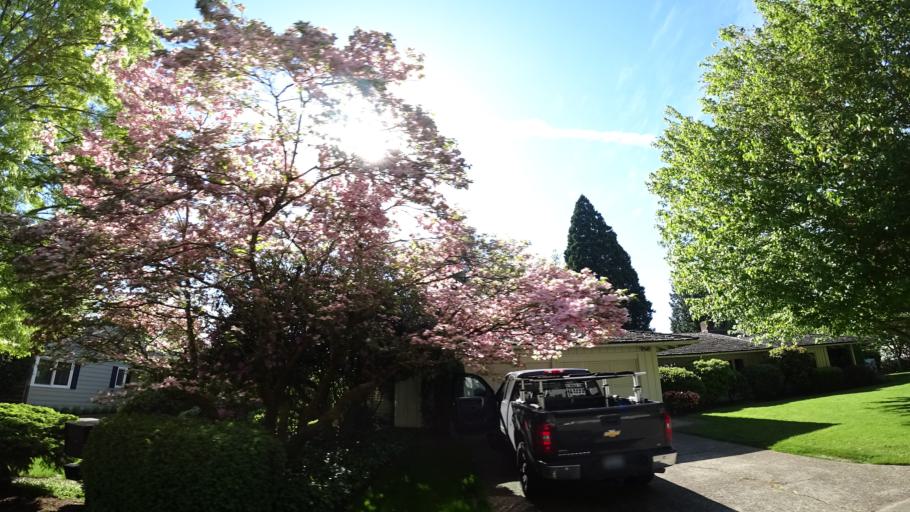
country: US
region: Oregon
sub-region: Washington County
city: Raleigh Hills
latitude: 45.4880
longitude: -122.7546
